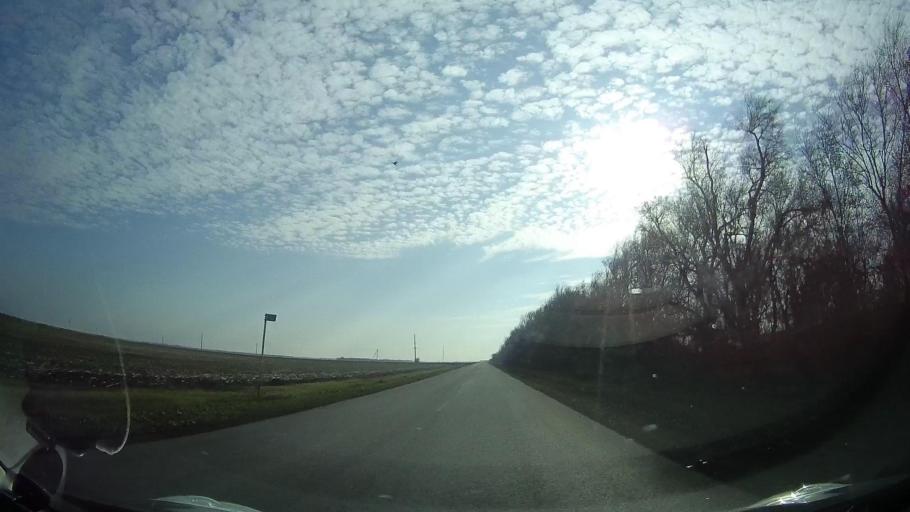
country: RU
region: Rostov
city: Veselyy
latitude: 46.9865
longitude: 40.7199
